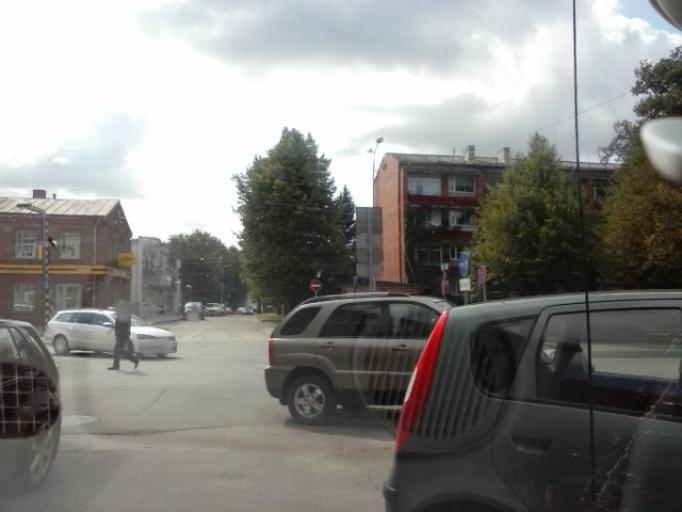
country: LV
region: Valmieras Rajons
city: Valmiera
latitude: 57.5375
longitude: 25.4116
